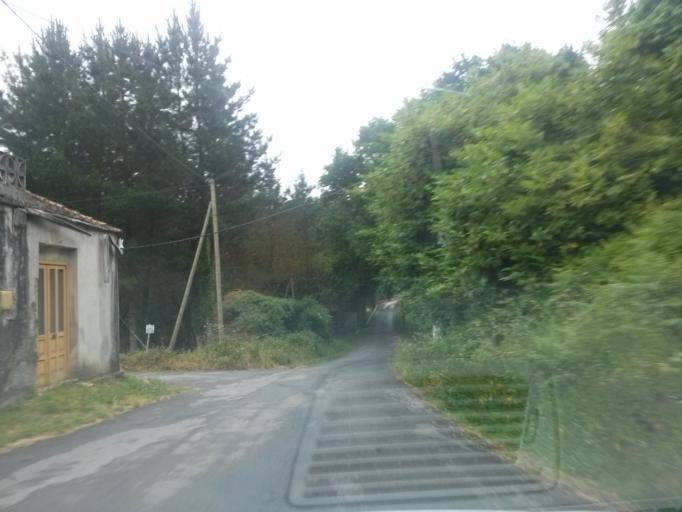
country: ES
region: Galicia
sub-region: Provincia de Lugo
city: Begonte
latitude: 43.1474
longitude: -7.6917
